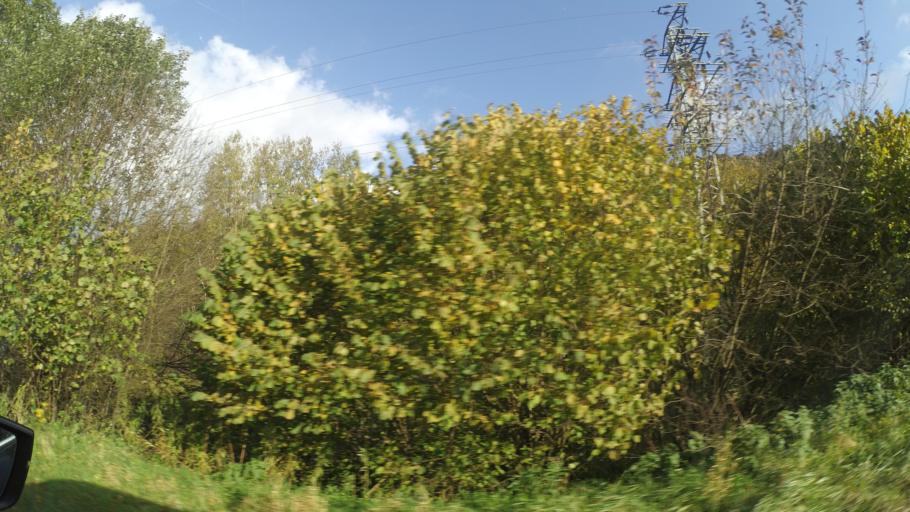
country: DE
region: Rheinland-Pfalz
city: Lemberg
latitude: 49.1779
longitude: 7.6521
